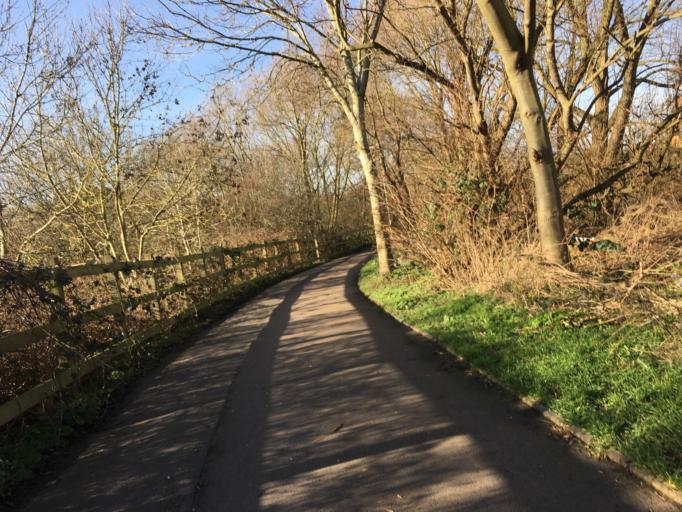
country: GB
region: England
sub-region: Warwickshire
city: Rugby
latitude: 52.3843
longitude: -1.2514
